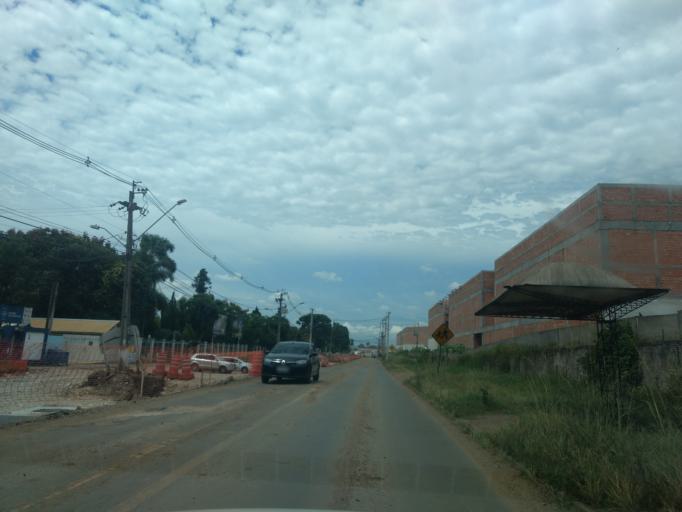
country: BR
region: Parana
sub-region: Pinhais
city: Pinhais
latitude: -25.4256
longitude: -49.2154
